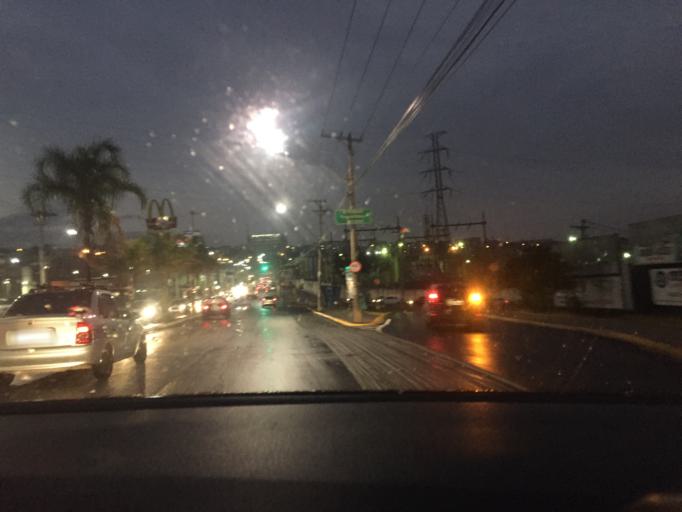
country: BR
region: Sao Paulo
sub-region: Varzea Paulista
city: Varzea Paulista
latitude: -23.2129
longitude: -46.8390
